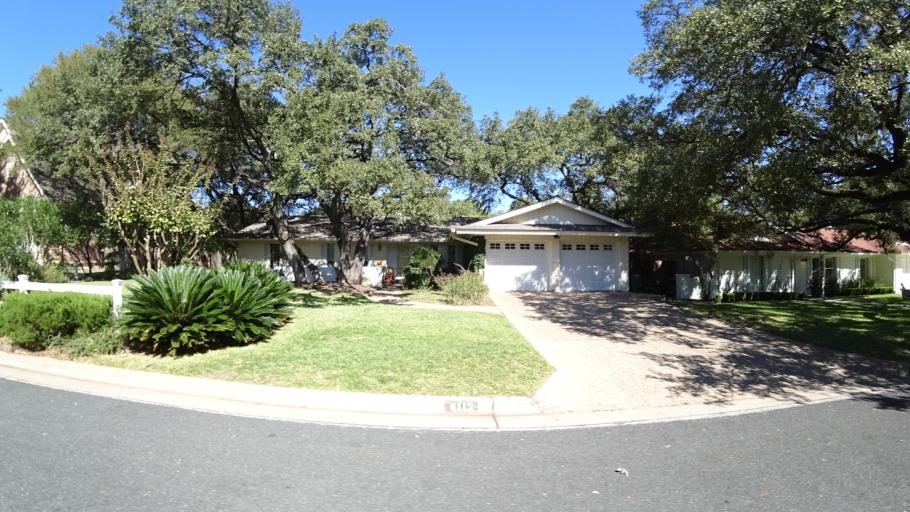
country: US
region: Texas
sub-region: Williamson County
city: Jollyville
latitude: 30.3683
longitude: -97.7615
